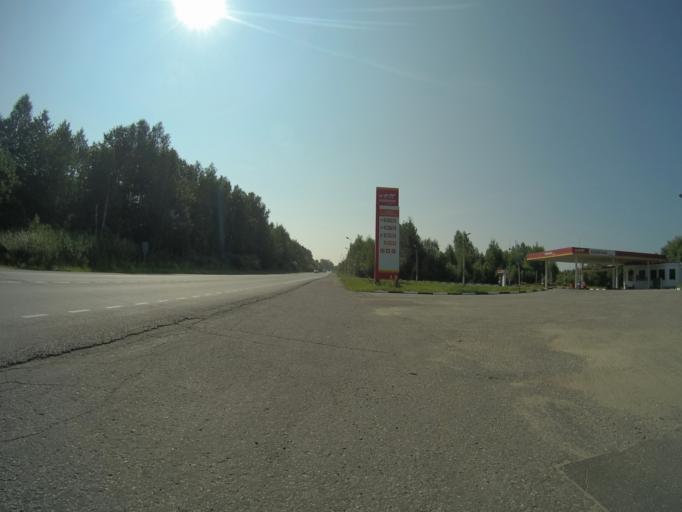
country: RU
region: Vladimir
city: Golovino
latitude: 55.9226
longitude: 40.6018
